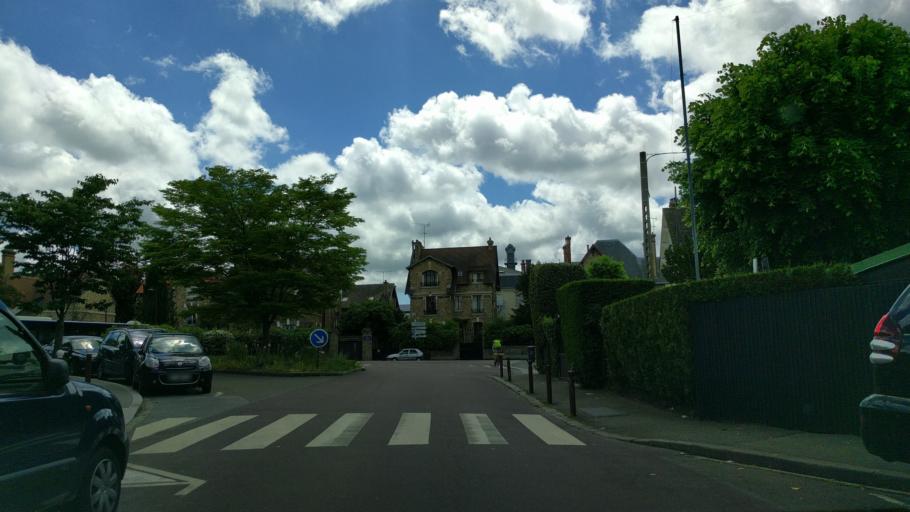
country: FR
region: Ile-de-France
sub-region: Departement des Yvelines
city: Le Chesnay
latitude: 48.8195
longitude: 2.1379
